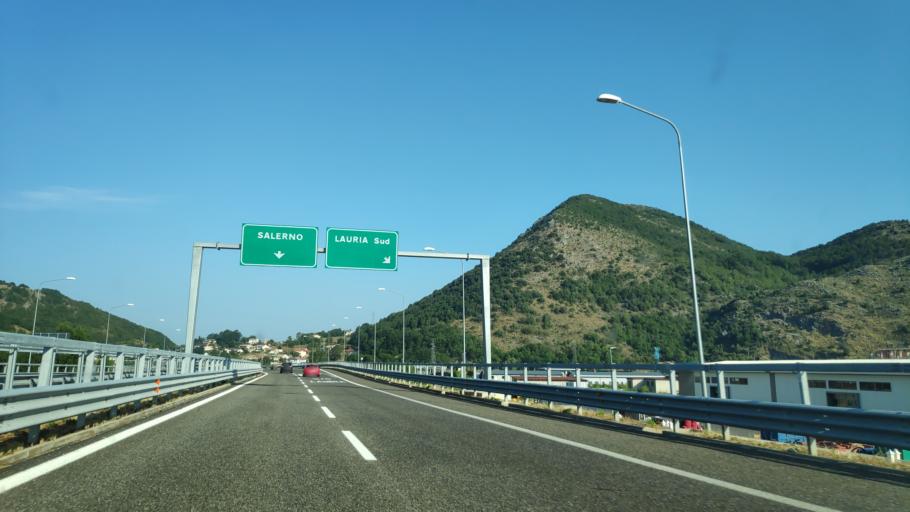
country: IT
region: Basilicate
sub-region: Provincia di Potenza
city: Lauria
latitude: 40.0161
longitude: 15.8933
